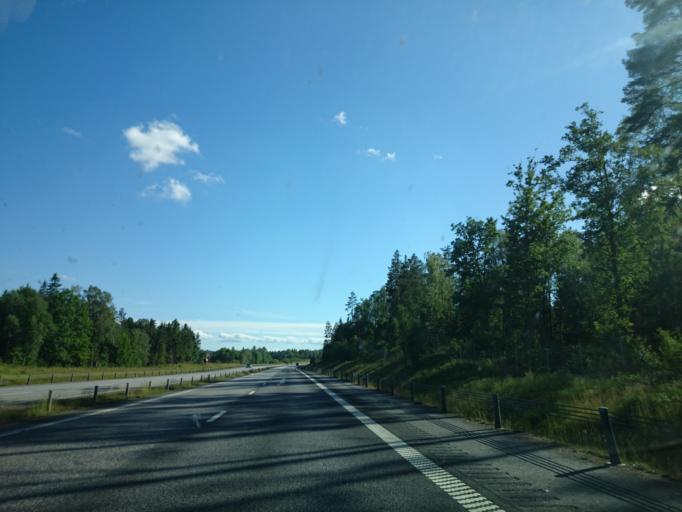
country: SE
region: Kronoberg
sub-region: Markaryds Kommun
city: Stromsnasbruk
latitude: 56.5282
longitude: 13.6856
